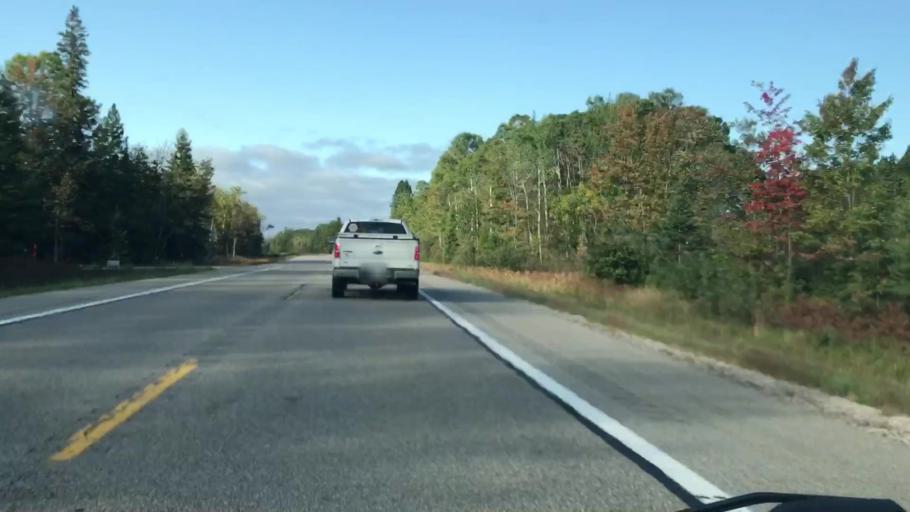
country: US
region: Michigan
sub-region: Luce County
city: Newberry
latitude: 46.3111
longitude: -85.2105
